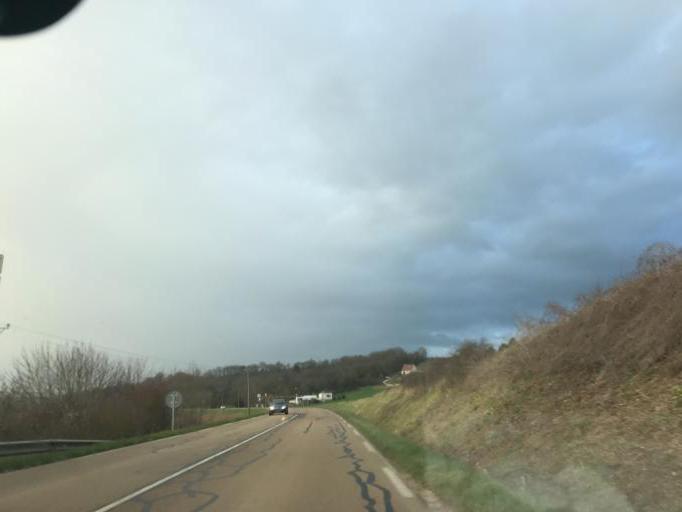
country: FR
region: Bourgogne
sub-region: Departement de l'Yonne
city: Fontenailles
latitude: 47.6170
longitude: 3.4966
